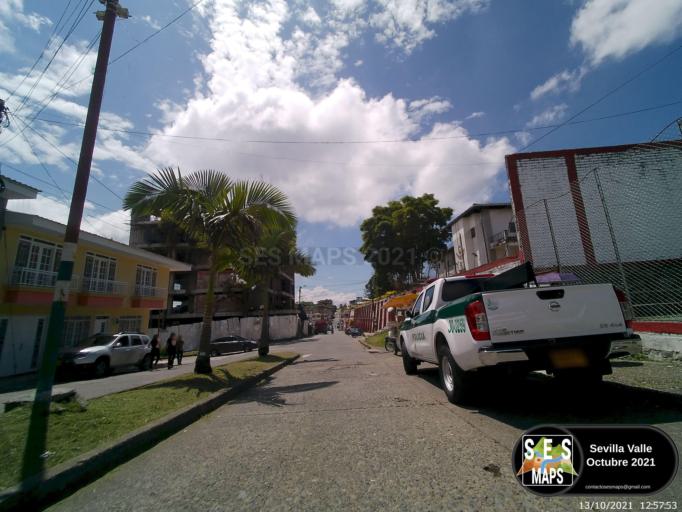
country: CO
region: Valle del Cauca
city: Sevilla
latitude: 4.2688
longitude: -75.9326
